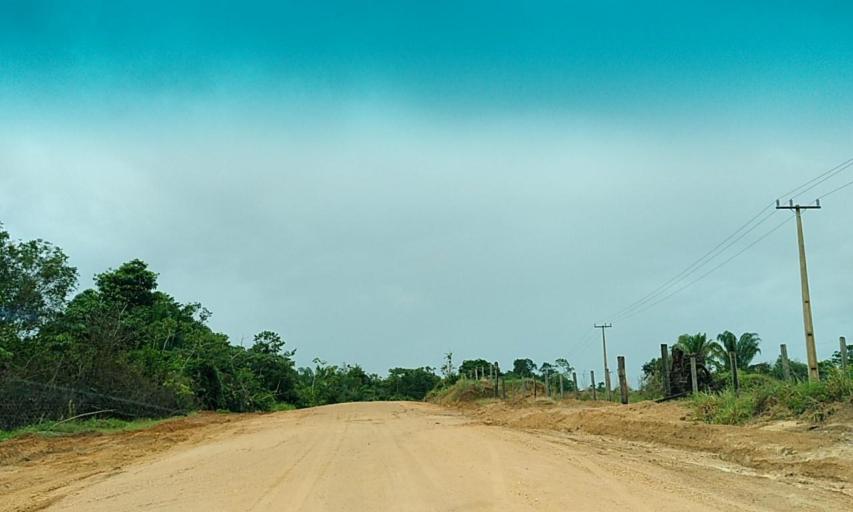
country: BR
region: Para
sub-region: Senador Jose Porfirio
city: Senador Jose Porfirio
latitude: -3.0593
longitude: -51.6680
